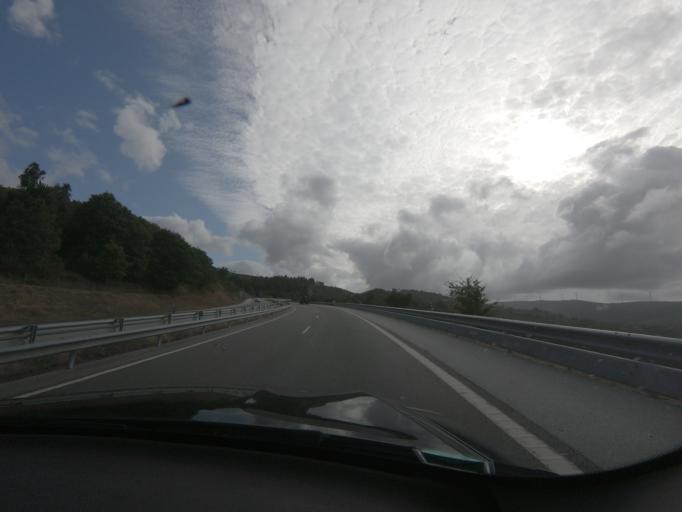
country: PT
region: Viseu
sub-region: Lamego
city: Lamego
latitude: 41.0734
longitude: -7.8208
